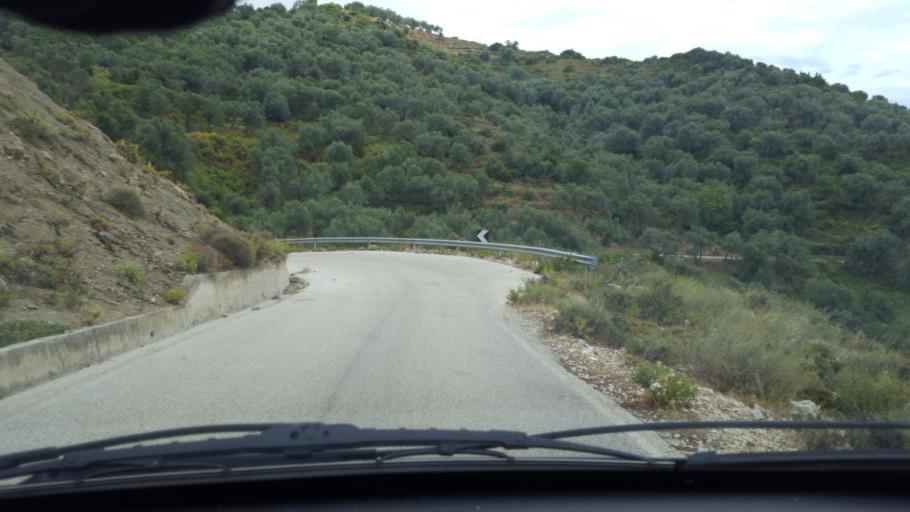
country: AL
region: Vlore
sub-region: Rrethi i Sarandes
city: Lukove
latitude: 39.9772
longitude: 19.9207
